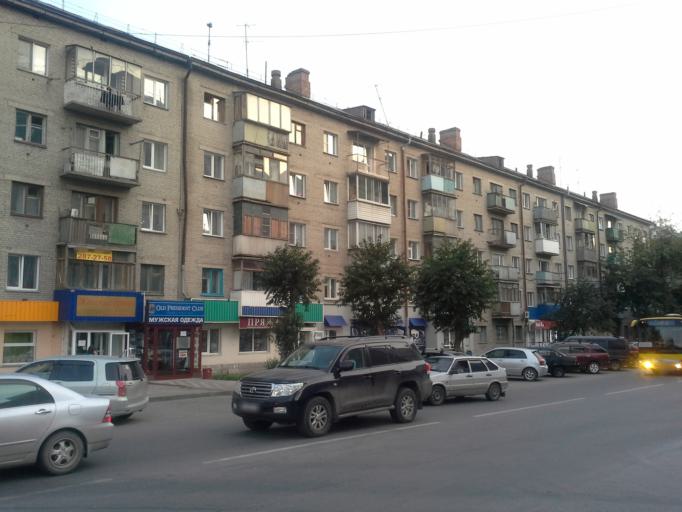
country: RU
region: Novosibirsk
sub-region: Novosibirskiy Rayon
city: Novosibirsk
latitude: 54.9807
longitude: 82.8999
